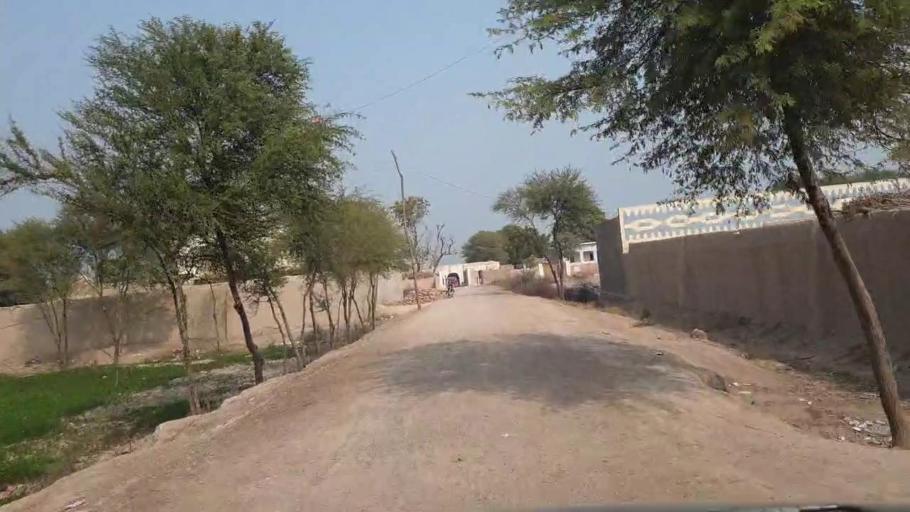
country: PK
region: Sindh
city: Bhit Shah
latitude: 25.8466
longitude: 68.4766
